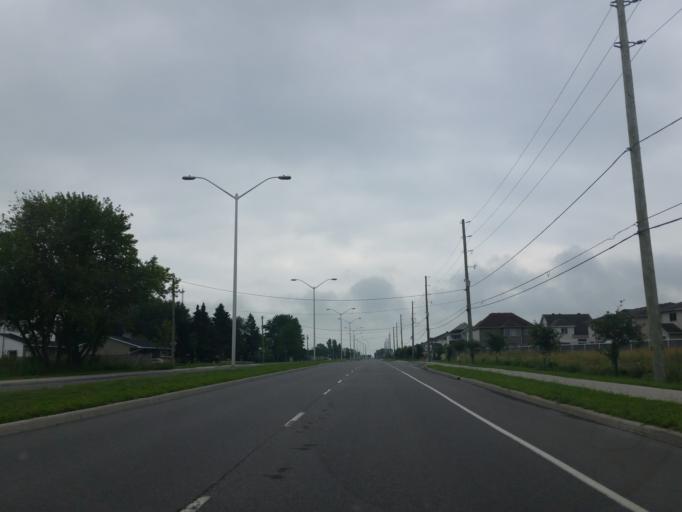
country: CA
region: Ontario
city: Clarence-Rockland
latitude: 45.4641
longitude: -75.4507
